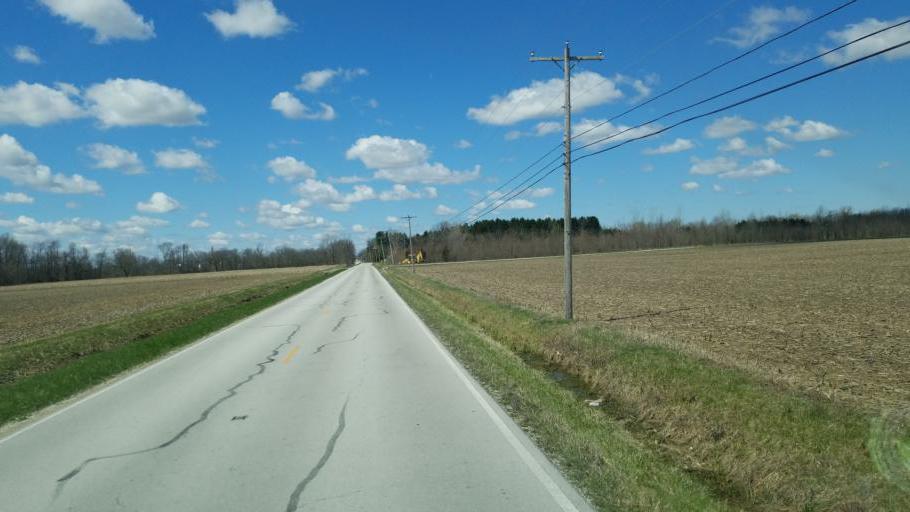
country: US
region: Ohio
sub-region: Sandusky County
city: Green Springs
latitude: 41.2569
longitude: -83.0703
